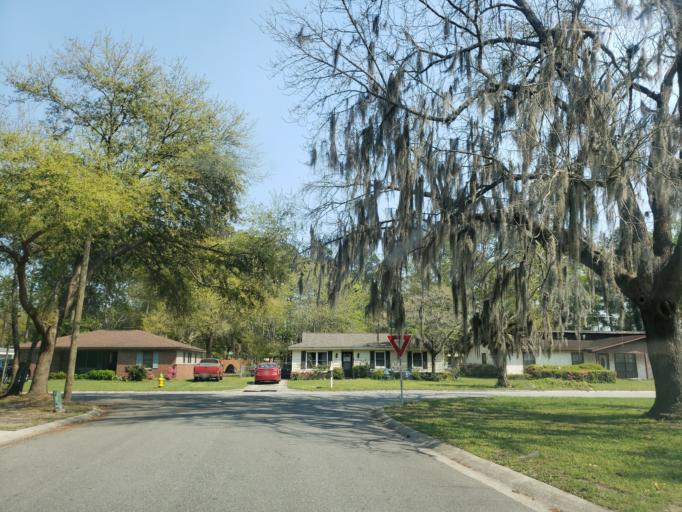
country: US
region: Georgia
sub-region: Chatham County
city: Isle of Hope
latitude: 32.0066
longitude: -81.0718
